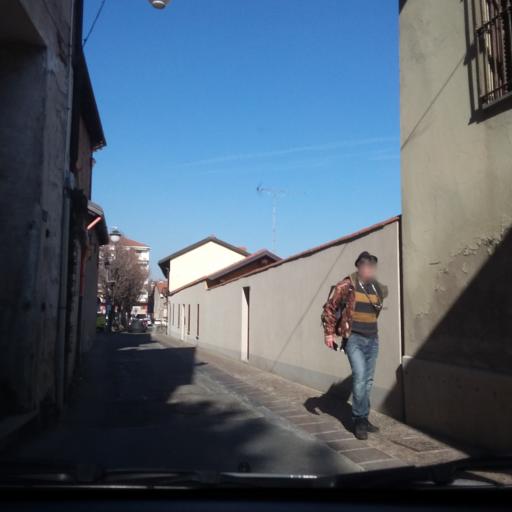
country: IT
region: Piedmont
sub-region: Provincia di Torino
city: Rivoli
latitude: 45.0676
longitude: 7.5146
